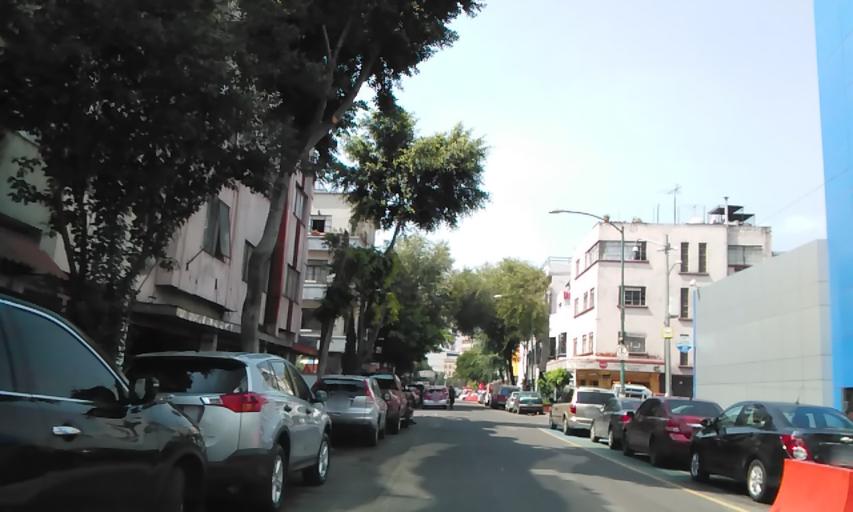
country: MX
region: Mexico City
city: Cuauhtemoc
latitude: 19.4387
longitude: -99.1549
